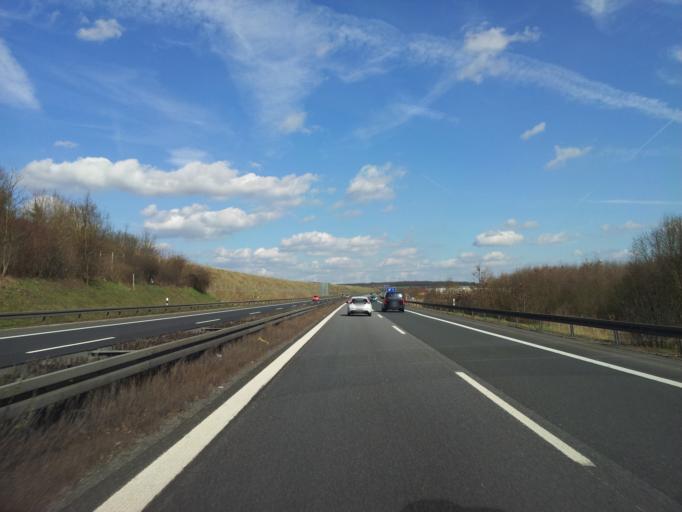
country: DE
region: Bavaria
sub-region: Regierungsbezirk Unterfranken
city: Sennfeld
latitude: 50.0272
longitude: 10.2498
